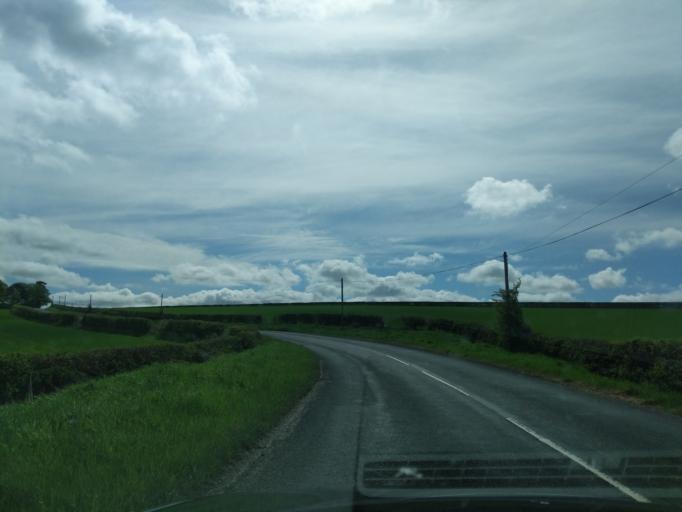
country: GB
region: Scotland
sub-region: The Scottish Borders
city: Saint Boswells
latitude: 55.6255
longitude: -2.5732
